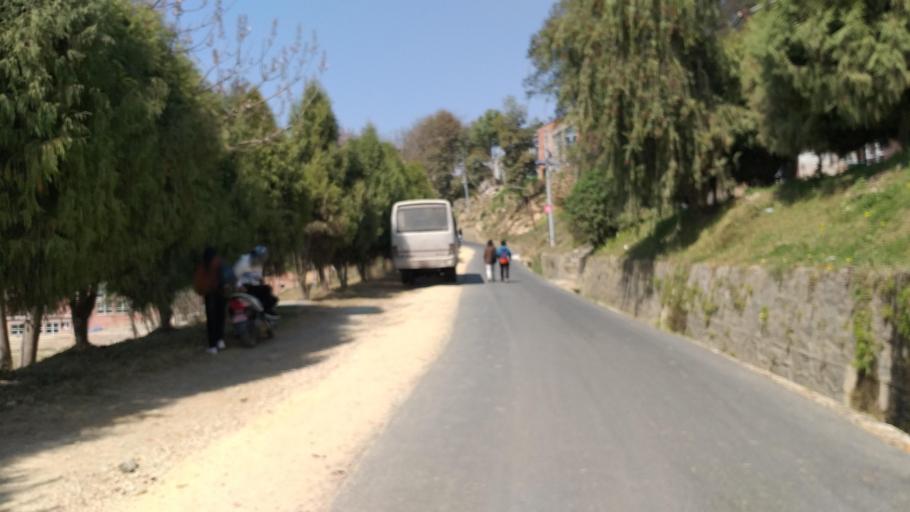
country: NP
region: Central Region
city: Banepa
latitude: 27.6180
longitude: 85.5377
